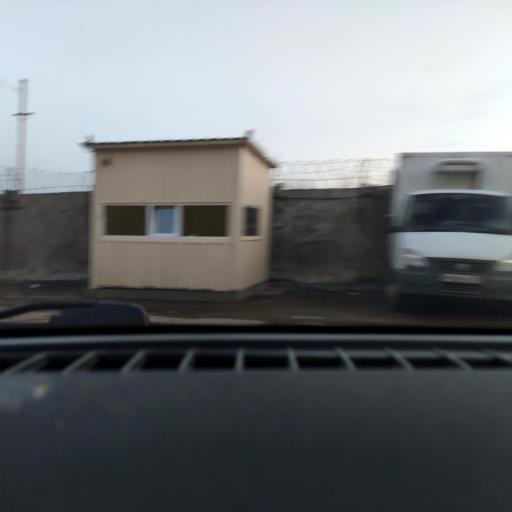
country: RU
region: Perm
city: Froly
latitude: 57.9567
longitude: 56.2567
